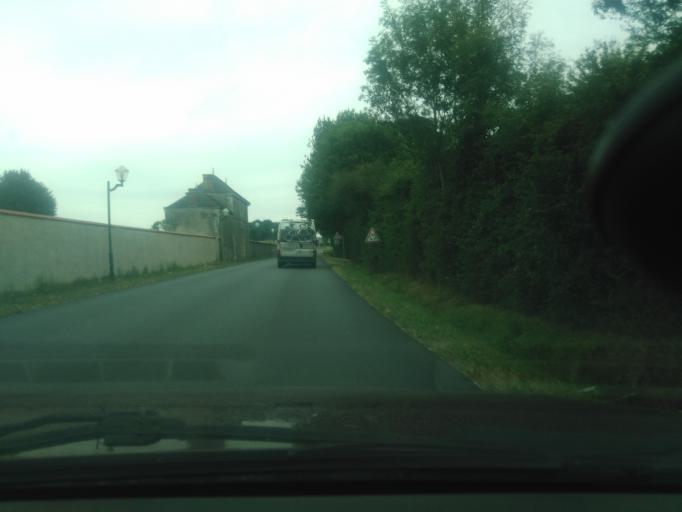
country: FR
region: Pays de la Loire
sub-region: Departement de la Vendee
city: Mouilleron-en-Pareds
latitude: 46.6777
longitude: -0.8421
